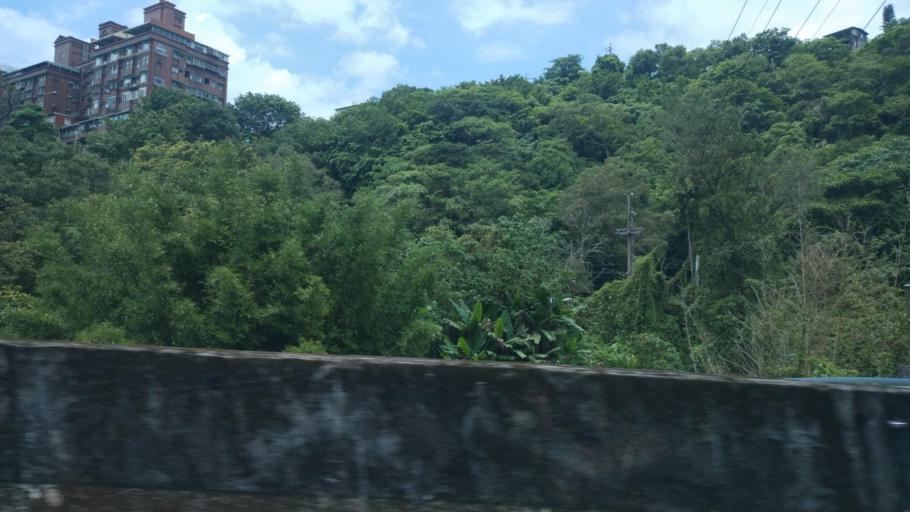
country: TW
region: Taipei
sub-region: Taipei
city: Banqiao
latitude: 24.9211
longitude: 121.4254
